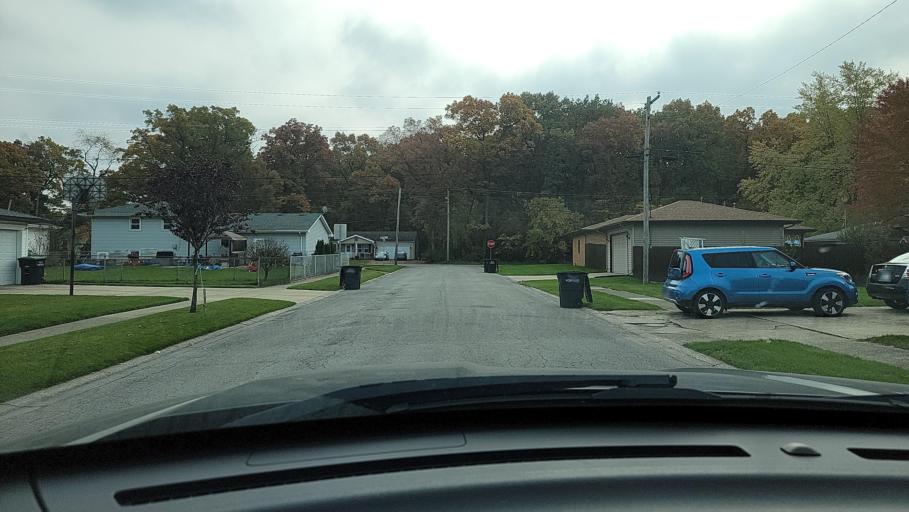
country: US
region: Indiana
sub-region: Porter County
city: Portage
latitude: 41.5876
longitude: -87.1590
